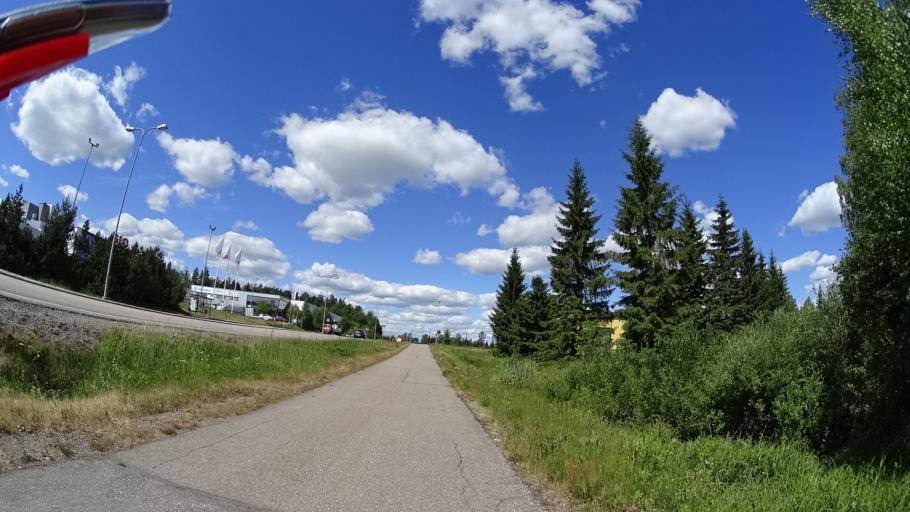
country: FI
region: Uusimaa
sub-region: Helsinki
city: Helsinki
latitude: 60.2947
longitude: 24.9087
